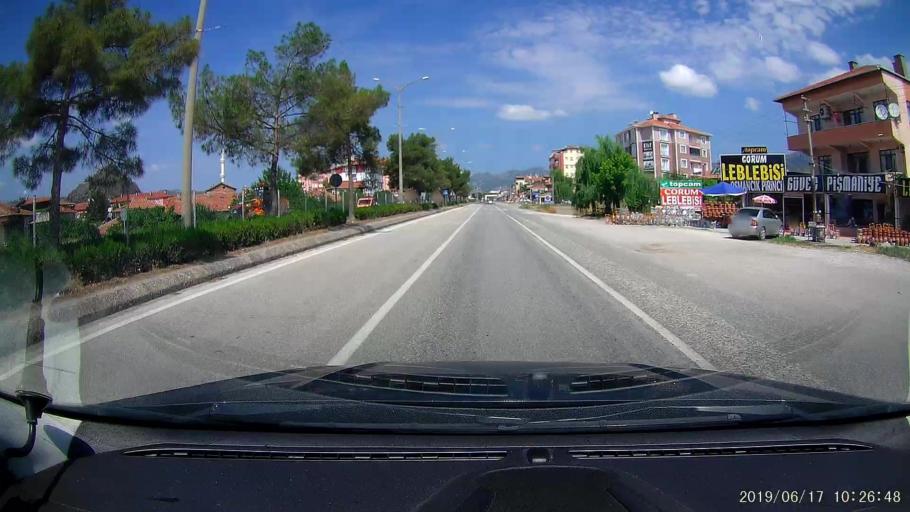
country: TR
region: Corum
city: Osmancik
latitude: 40.9754
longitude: 34.8146
